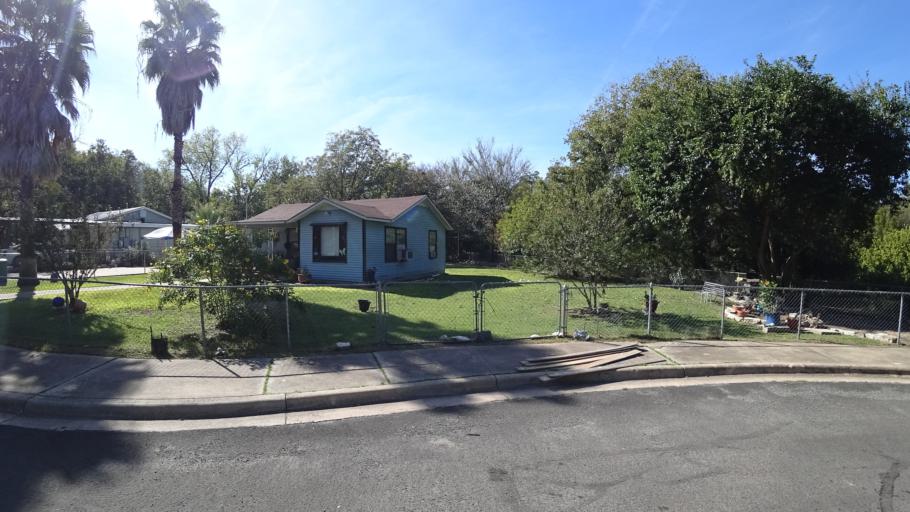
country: US
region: Texas
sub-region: Travis County
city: Austin
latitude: 30.2601
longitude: -97.6872
